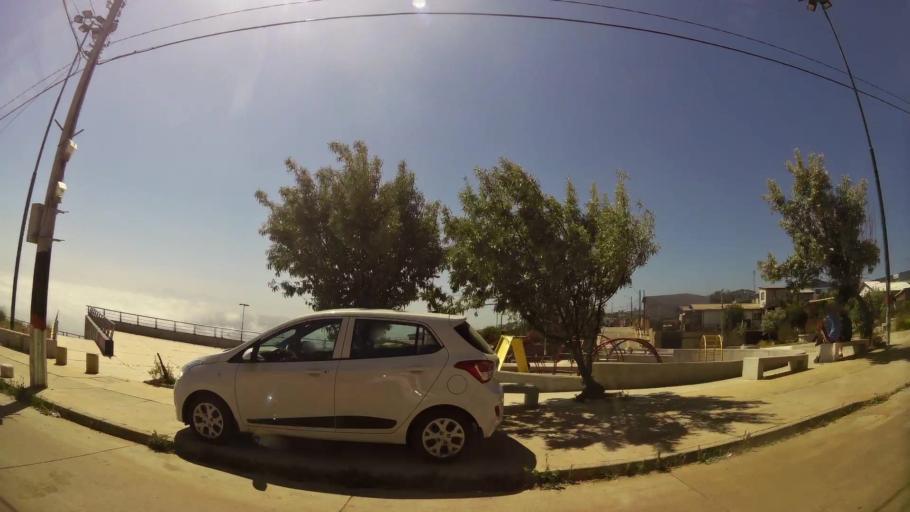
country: CL
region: Valparaiso
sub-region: Provincia de Valparaiso
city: Valparaiso
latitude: -33.0499
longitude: -71.6470
